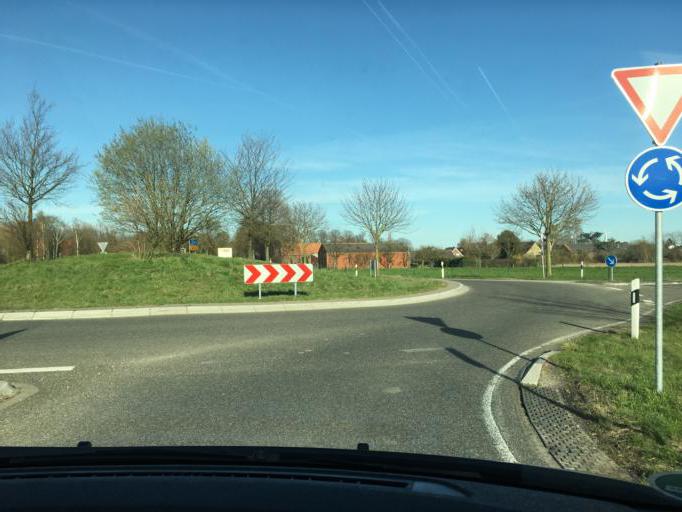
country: DE
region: North Rhine-Westphalia
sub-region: Regierungsbezirk Dusseldorf
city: Korschenbroich
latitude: 51.1858
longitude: 6.5540
